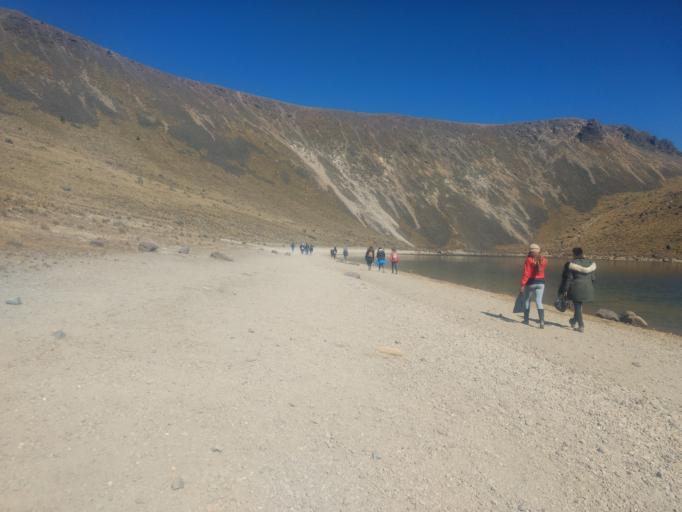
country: MX
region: Mexico
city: Cerro La Calera
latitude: 19.1117
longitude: -99.7597
